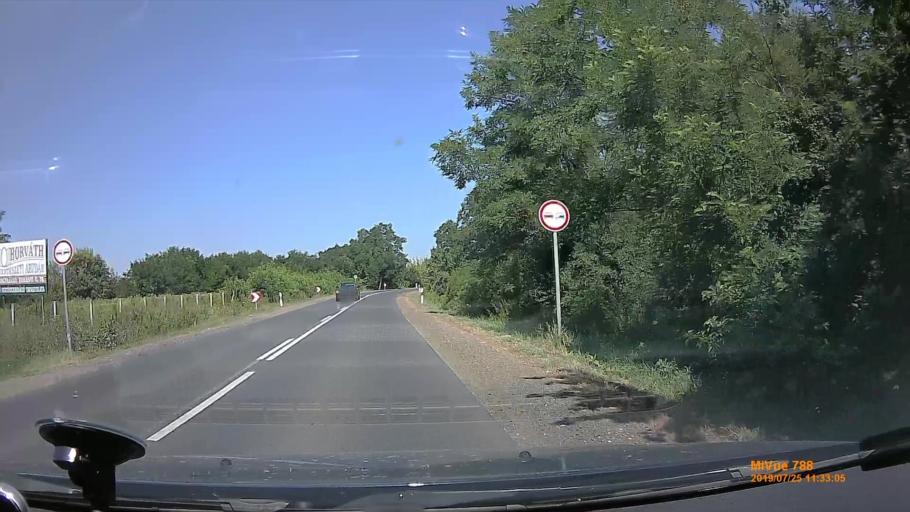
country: HU
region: Szabolcs-Szatmar-Bereg
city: Nyiregyhaza
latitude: 47.9233
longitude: 21.7673
